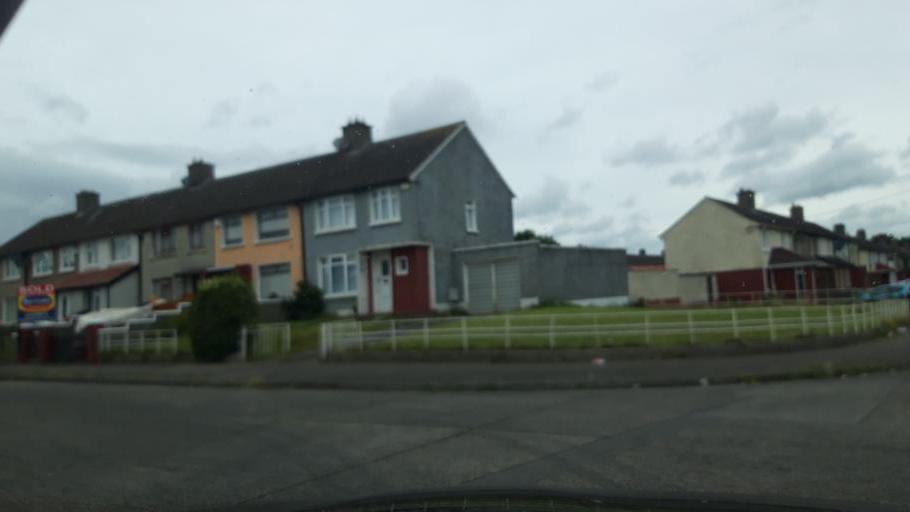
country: IE
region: Leinster
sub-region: Dublin City
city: Finglas
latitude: 53.3830
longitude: -6.3035
